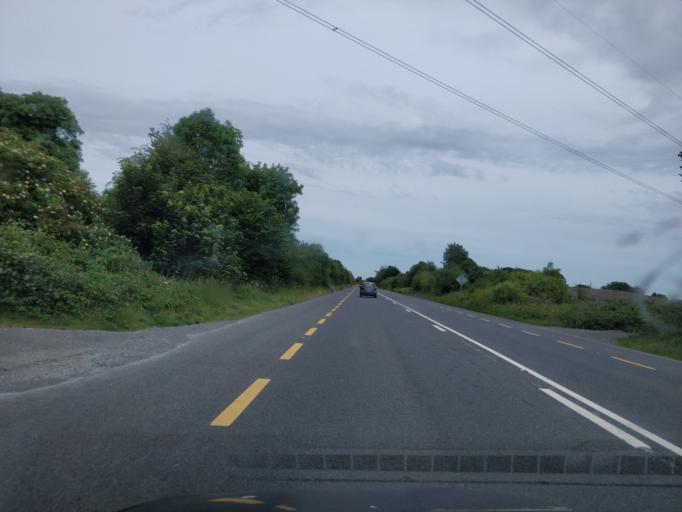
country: IE
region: Leinster
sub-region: Uibh Fhaili
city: Birr
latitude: 53.1330
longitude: -7.8572
